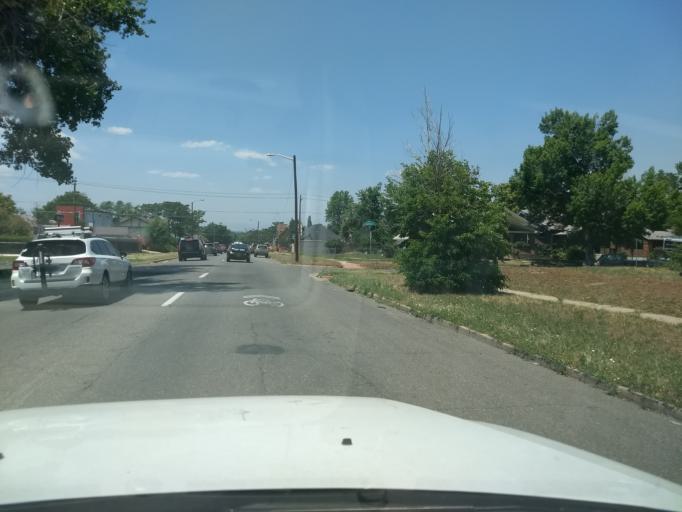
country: US
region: Colorado
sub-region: Denver County
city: Denver
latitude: 39.7620
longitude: -104.9570
